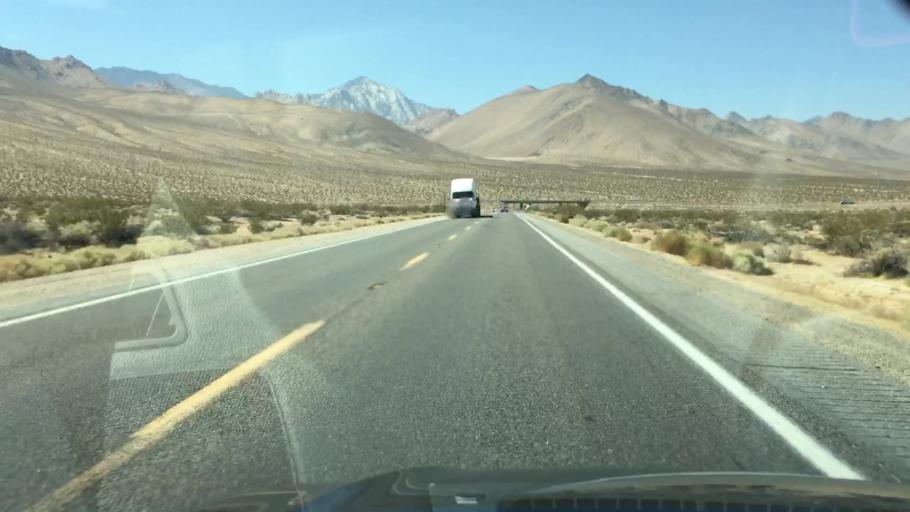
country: US
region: California
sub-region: Kern County
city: Inyokern
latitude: 35.6907
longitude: -117.8605
